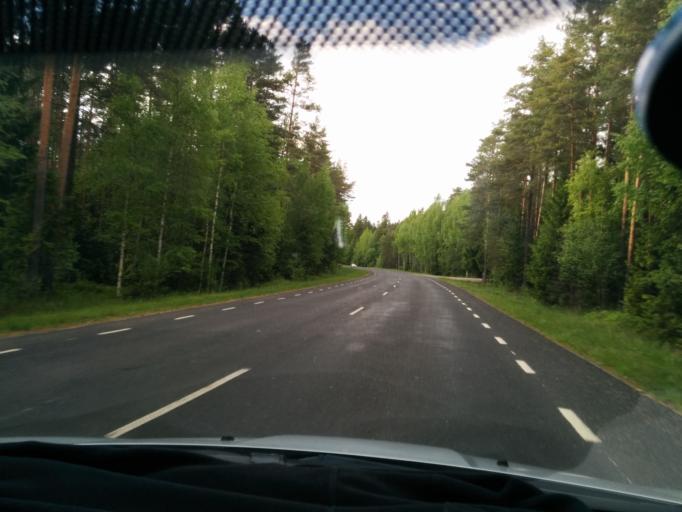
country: EE
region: Harju
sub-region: Loksa linn
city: Loksa
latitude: 59.5481
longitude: 25.7370
